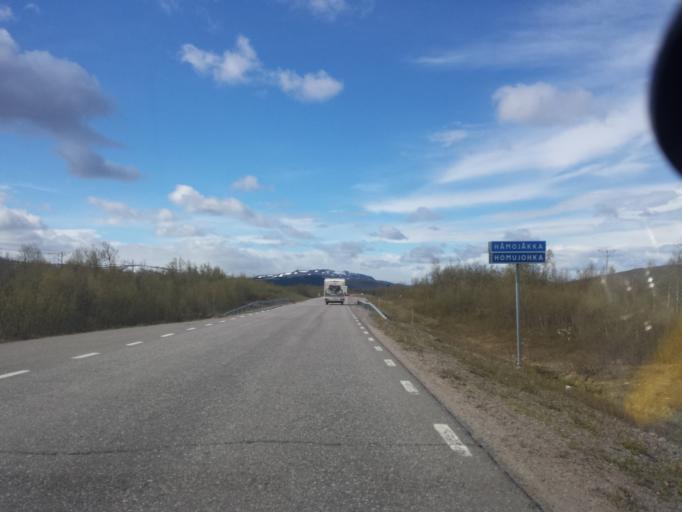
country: SE
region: Norrbotten
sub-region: Kiruna Kommun
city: Kiruna
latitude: 68.0069
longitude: 19.8491
